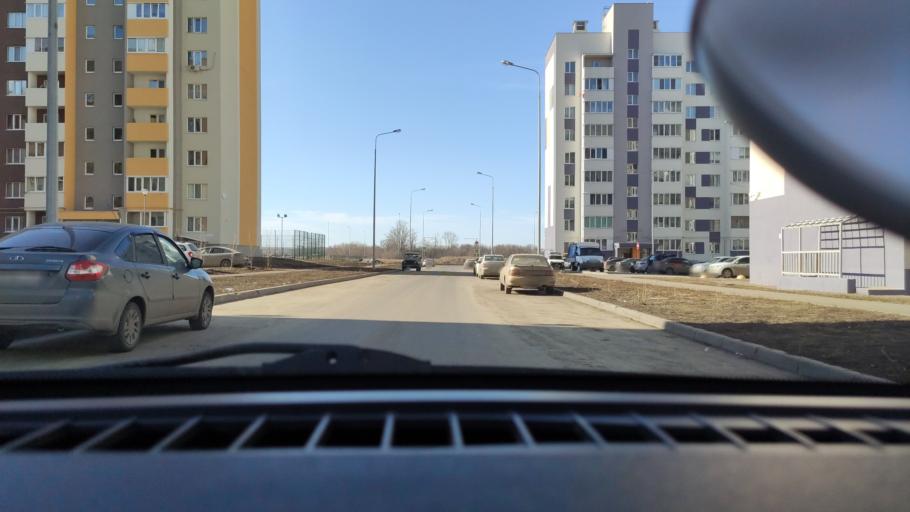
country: RU
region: Samara
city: Samara
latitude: 53.0928
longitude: 50.1601
